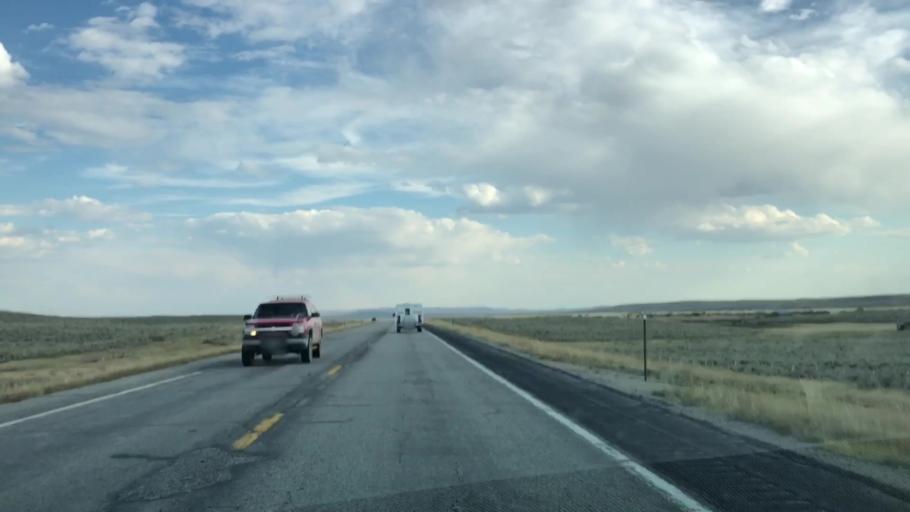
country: US
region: Wyoming
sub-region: Sublette County
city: Pinedale
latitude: 43.0507
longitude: -110.1515
